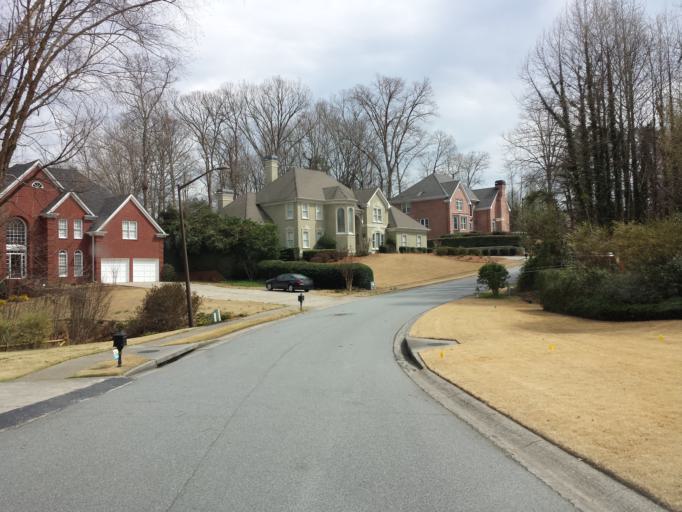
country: US
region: Georgia
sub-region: Cobb County
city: Vinings
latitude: 33.9486
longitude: -84.4607
